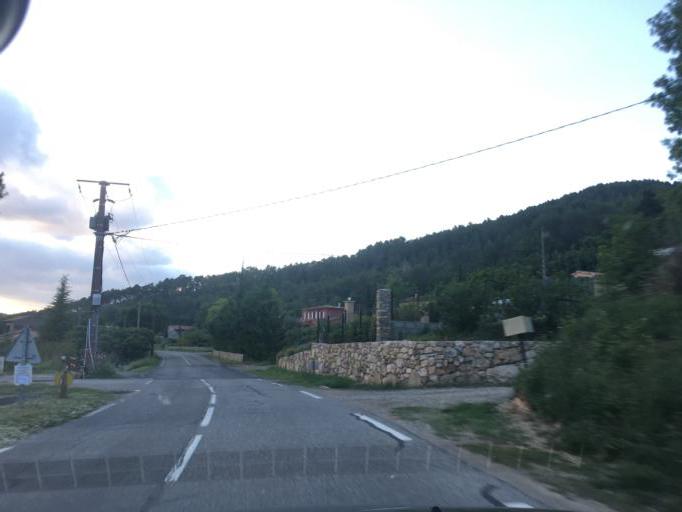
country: FR
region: Provence-Alpes-Cote d'Azur
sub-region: Departement du Var
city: Salernes
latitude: 43.5429
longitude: 6.2562
